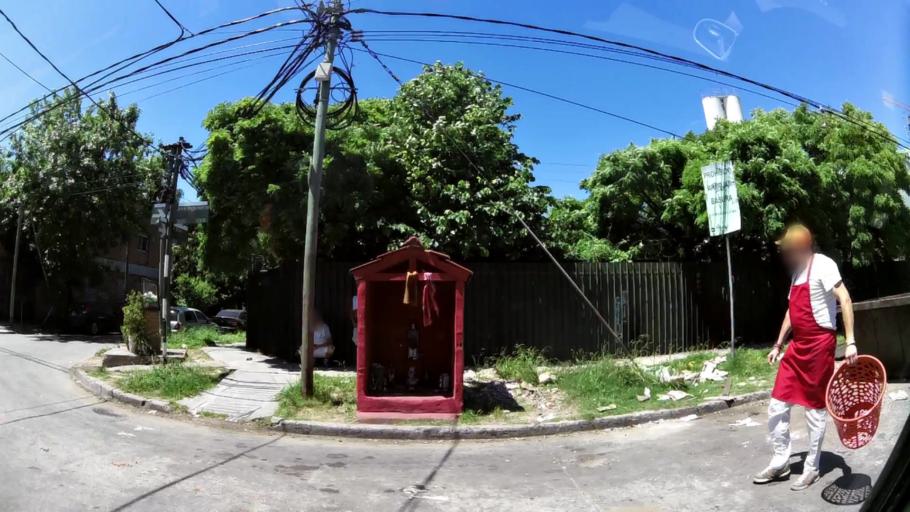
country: AR
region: Buenos Aires
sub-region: Partido de Vicente Lopez
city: Olivos
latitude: -34.5137
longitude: -58.5170
